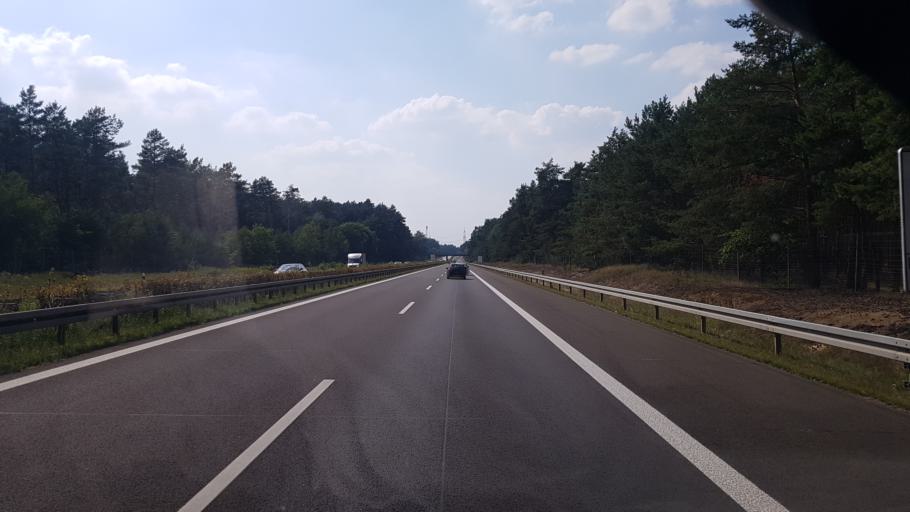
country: DE
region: Brandenburg
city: Kolkwitz
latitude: 51.7275
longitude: 14.2046
